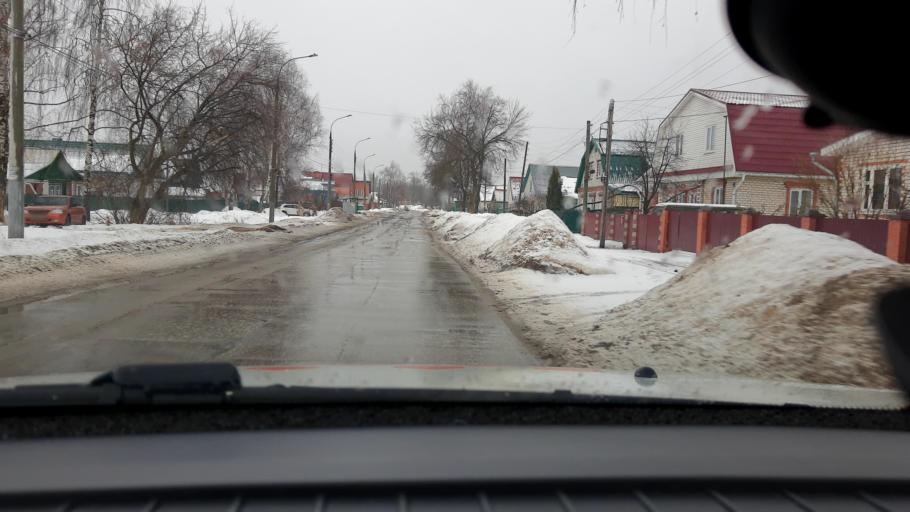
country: RU
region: Nizjnij Novgorod
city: Kstovo
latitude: 56.1799
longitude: 44.1738
